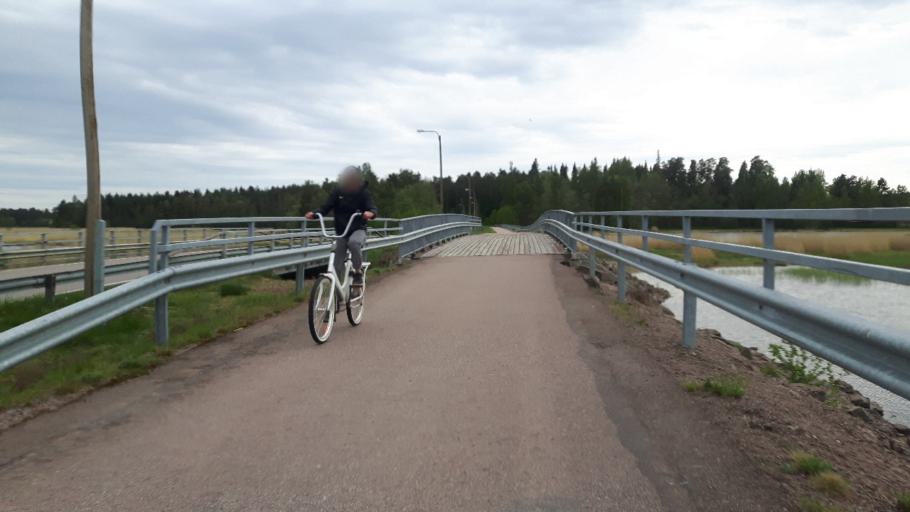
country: FI
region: Kymenlaakso
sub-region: Kotka-Hamina
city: Hamina
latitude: 60.5504
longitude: 27.2286
